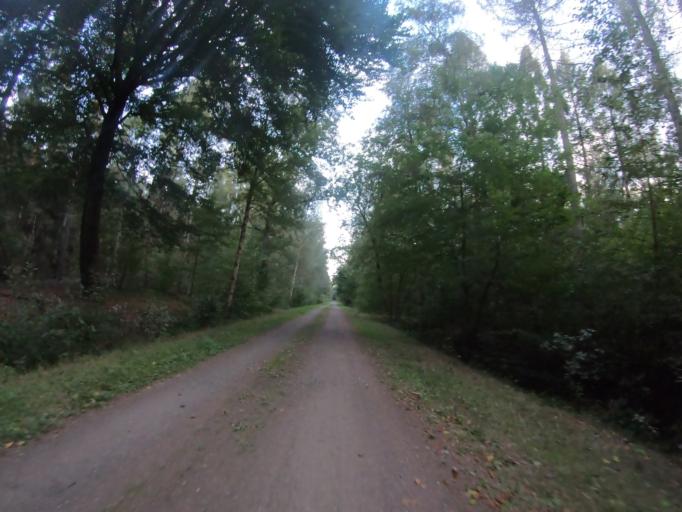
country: DE
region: Lower Saxony
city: Gifhorn
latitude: 52.5087
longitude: 10.5633
